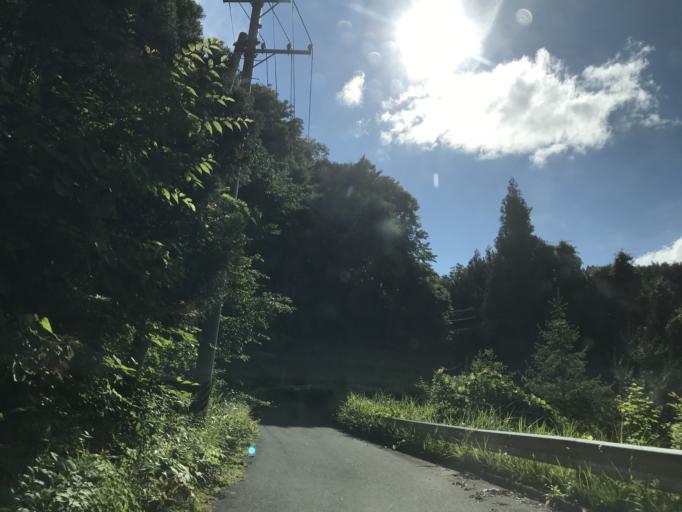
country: JP
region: Iwate
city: Ichinoseki
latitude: 38.8917
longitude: 140.9068
